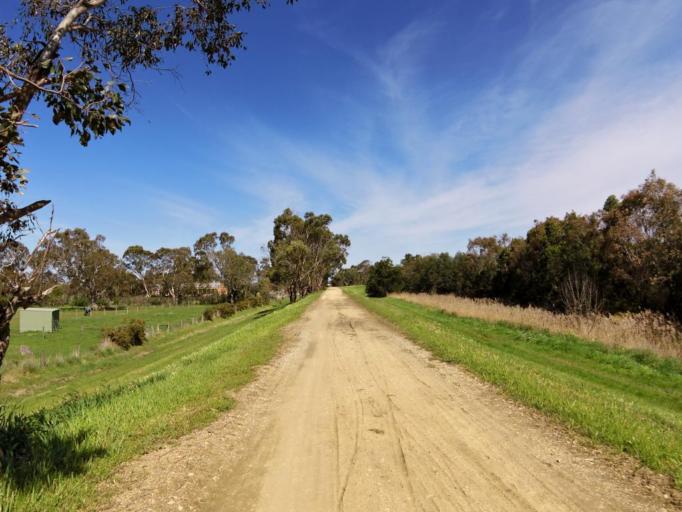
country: AU
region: Victoria
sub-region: Greater Dandenong
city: Keysborough
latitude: -38.0348
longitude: 145.1830
